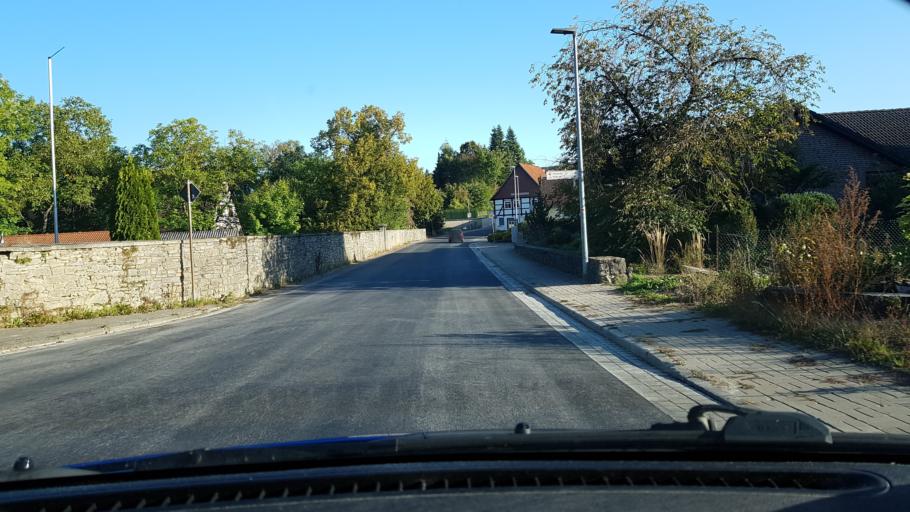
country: DE
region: Lower Saxony
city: Messenkamp
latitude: 52.2333
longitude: 9.4247
